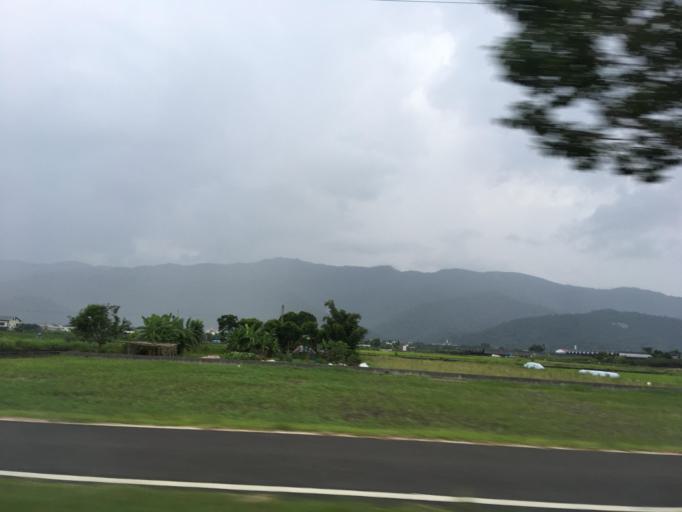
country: TW
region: Taiwan
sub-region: Yilan
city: Yilan
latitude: 24.6771
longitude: 121.6502
